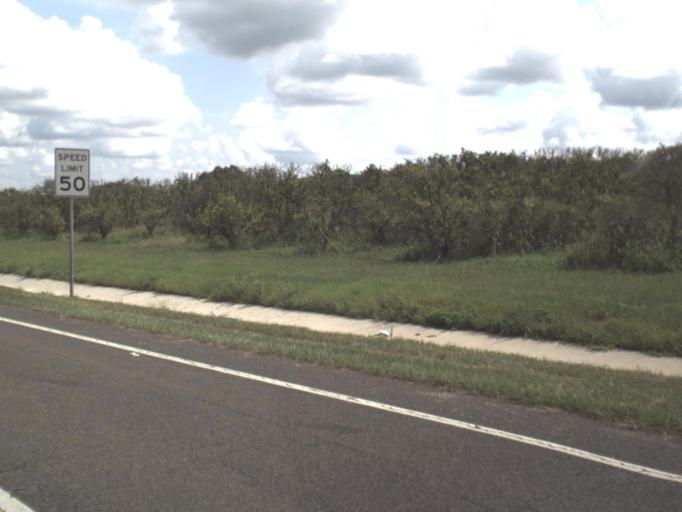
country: US
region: Florida
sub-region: Pasco County
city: Dade City
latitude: 28.3294
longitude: -82.1874
